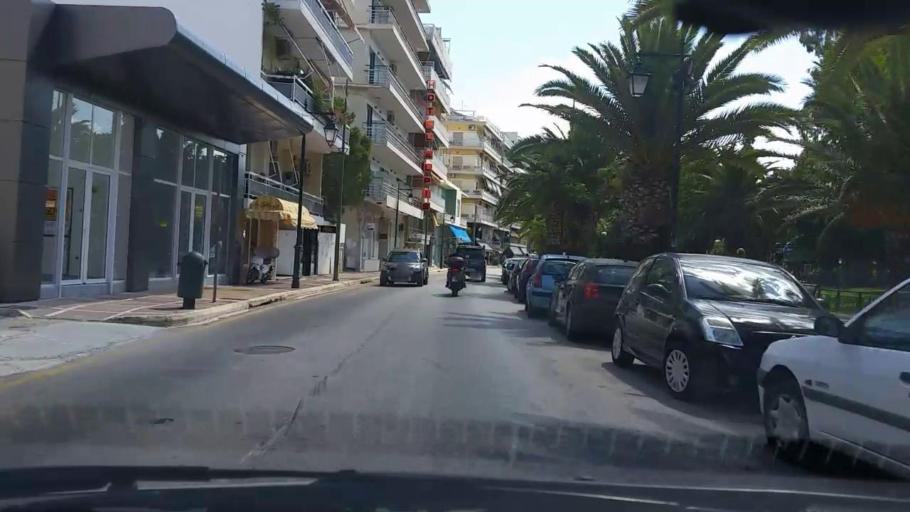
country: GR
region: Peloponnese
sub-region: Nomos Korinthias
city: Loutraki
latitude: 37.9802
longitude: 22.9750
